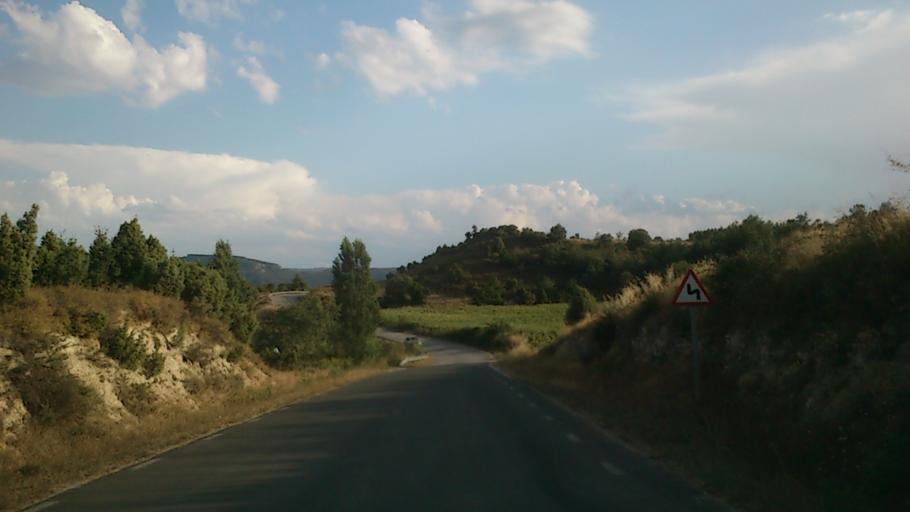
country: ES
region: Castille and Leon
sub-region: Provincia de Burgos
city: Frias
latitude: 42.8078
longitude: -3.2542
